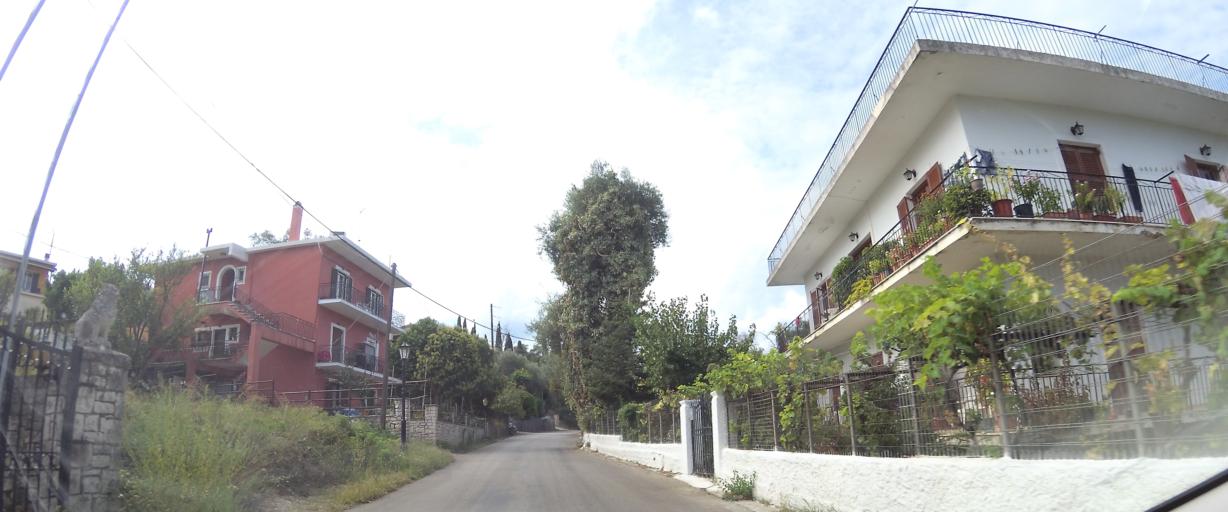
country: GR
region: Ionian Islands
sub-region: Nomos Kerkyras
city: Kontokali
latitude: 39.6918
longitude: 19.8224
